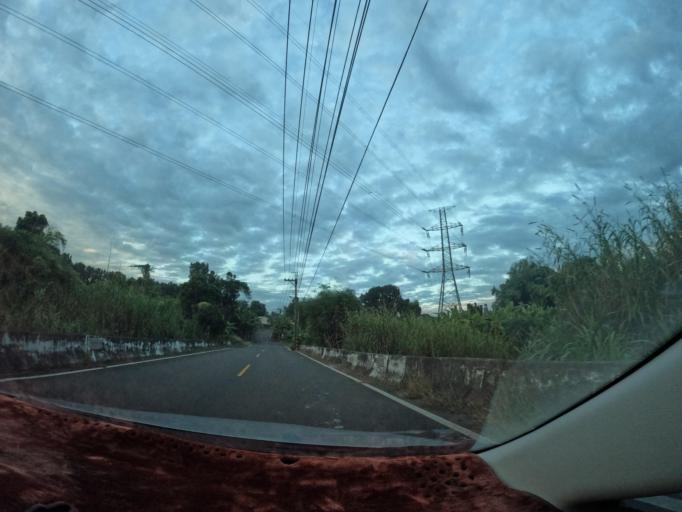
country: TW
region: Taiwan
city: Yujing
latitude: 23.0328
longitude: 120.4157
